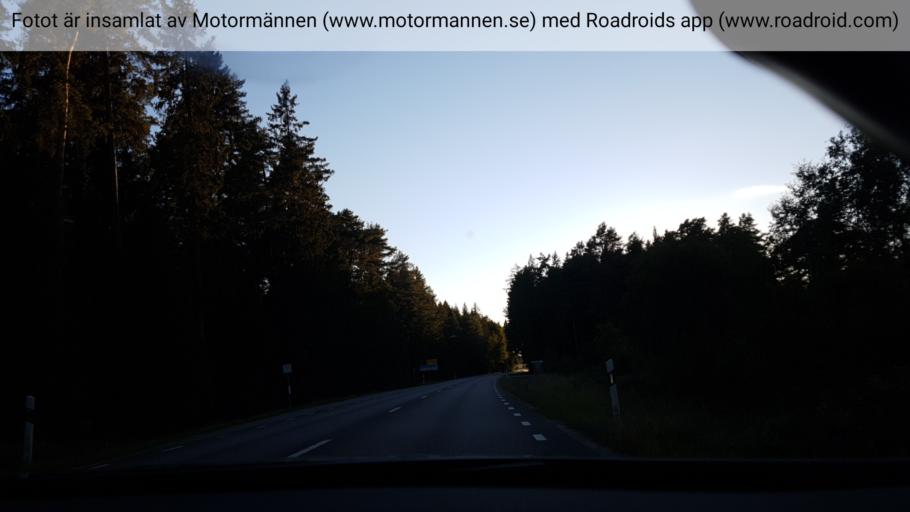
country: SE
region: Vaestra Goetaland
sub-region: Tibro Kommun
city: Tibro
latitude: 58.3432
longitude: 14.1580
